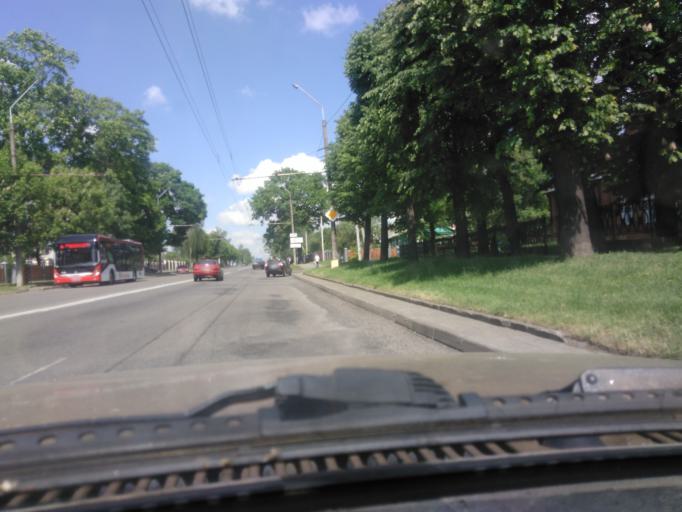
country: BY
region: Mogilev
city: Mahilyow
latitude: 53.9297
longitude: 30.3382
